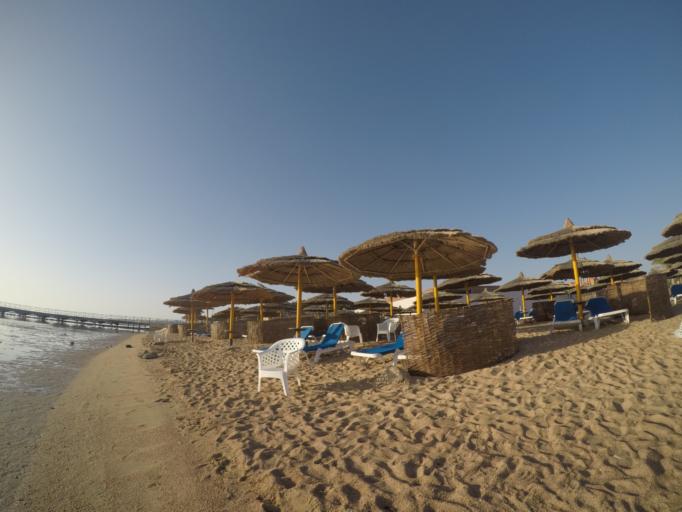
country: EG
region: Red Sea
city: Makadi Bay
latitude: 27.0925
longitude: 33.8528
